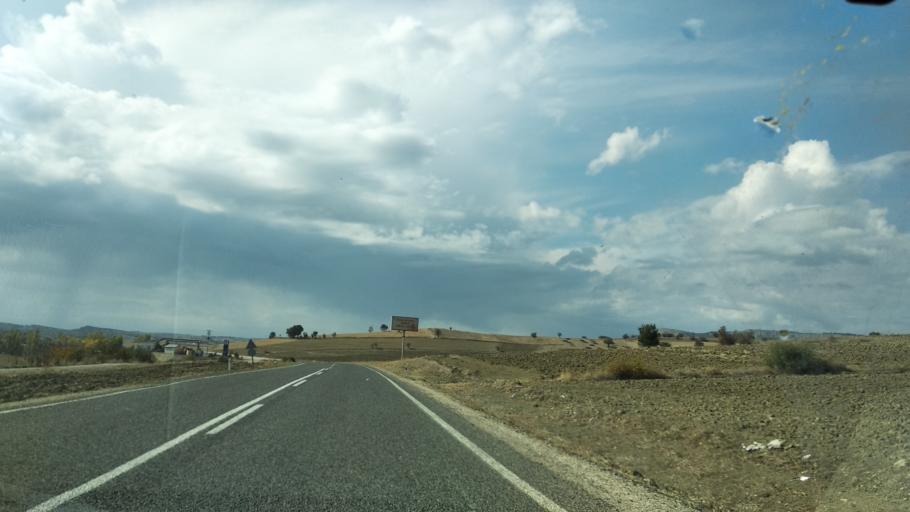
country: TR
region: Bolu
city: Seben
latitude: 40.4022
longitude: 31.5636
